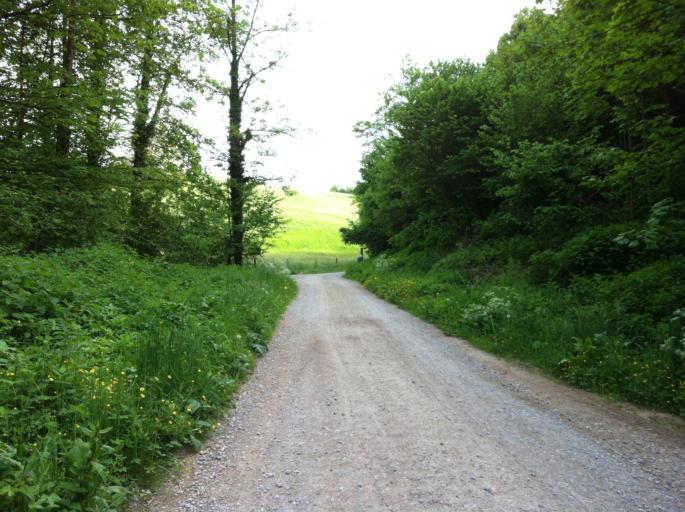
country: DE
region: Baden-Wuerttemberg
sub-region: Freiburg Region
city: Maulburg
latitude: 47.6092
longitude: 7.7930
